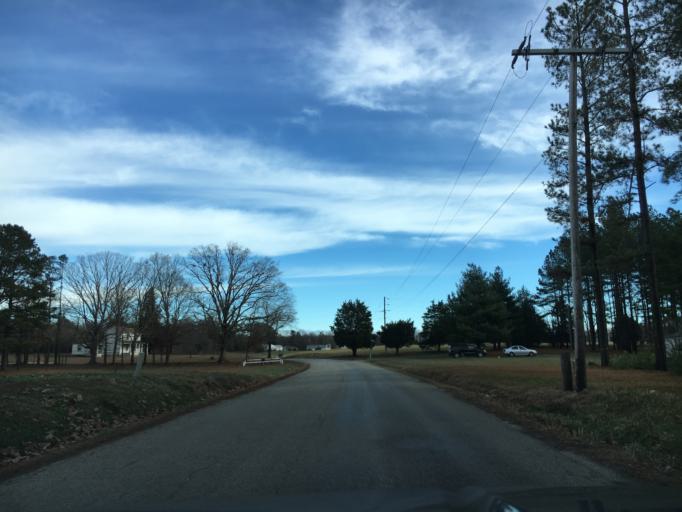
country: US
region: Virginia
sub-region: Nottoway County
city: Crewe
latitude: 37.2391
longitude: -78.2325
